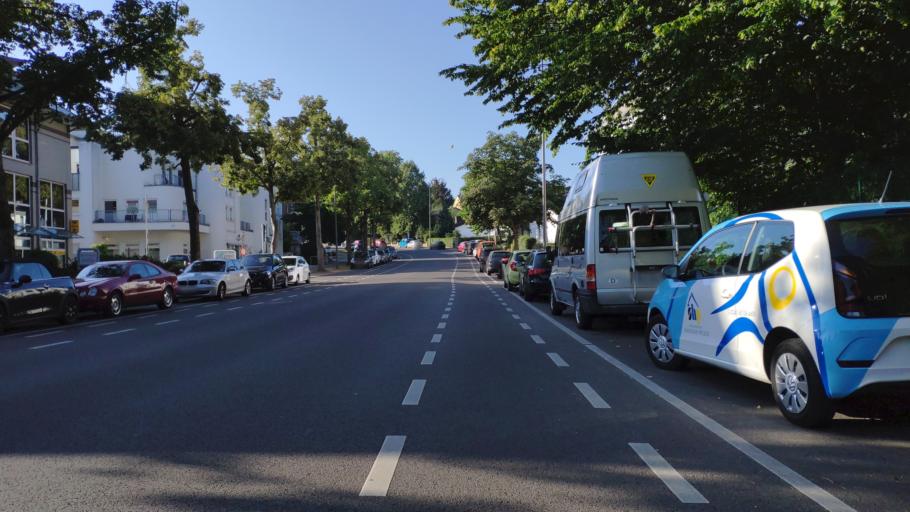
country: DE
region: North Rhine-Westphalia
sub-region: Regierungsbezirk Koln
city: Aachen
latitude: 50.7527
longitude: 6.0857
